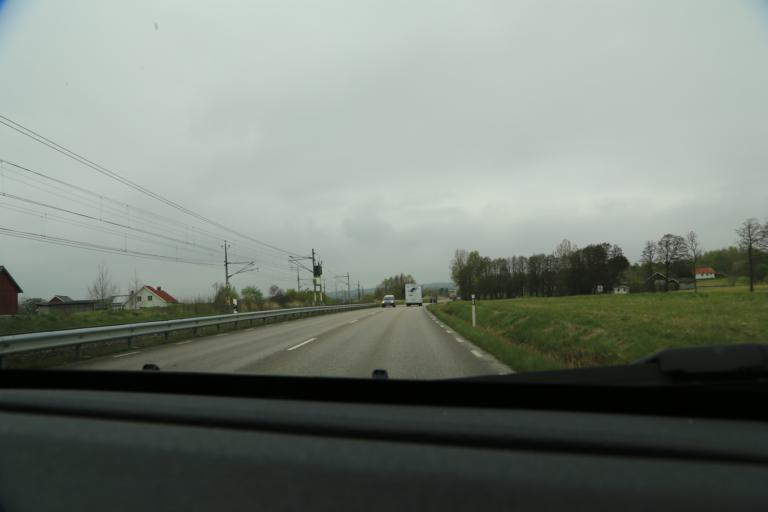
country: SE
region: Halland
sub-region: Varbergs Kommun
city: Varberg
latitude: 57.2102
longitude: 12.2218
